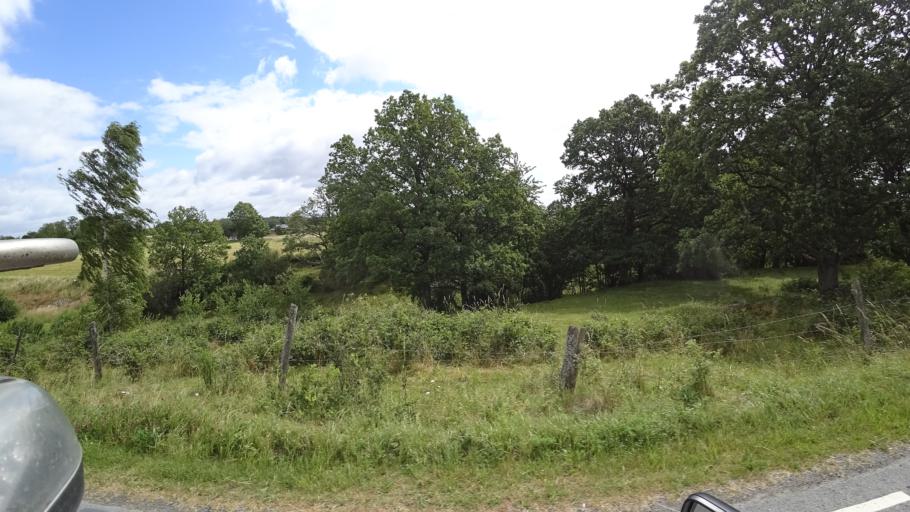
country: SE
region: Skane
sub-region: Kristianstads Kommun
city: Degeberga
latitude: 55.7307
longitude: 14.0005
